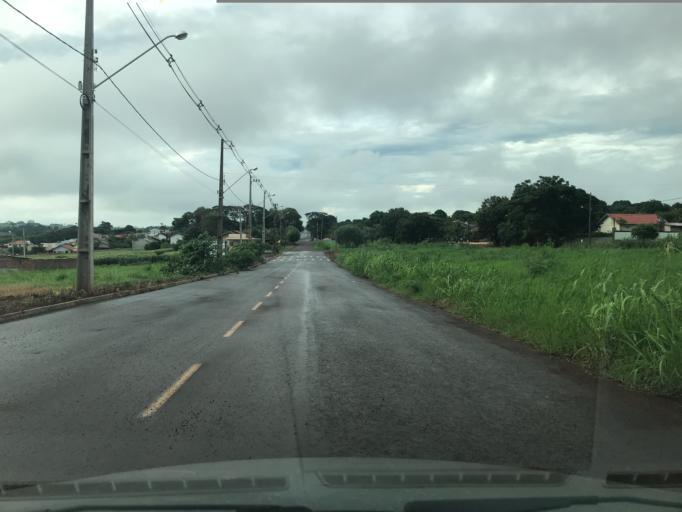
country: BR
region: Parana
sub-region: Palotina
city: Palotina
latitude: -24.2954
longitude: -53.8478
